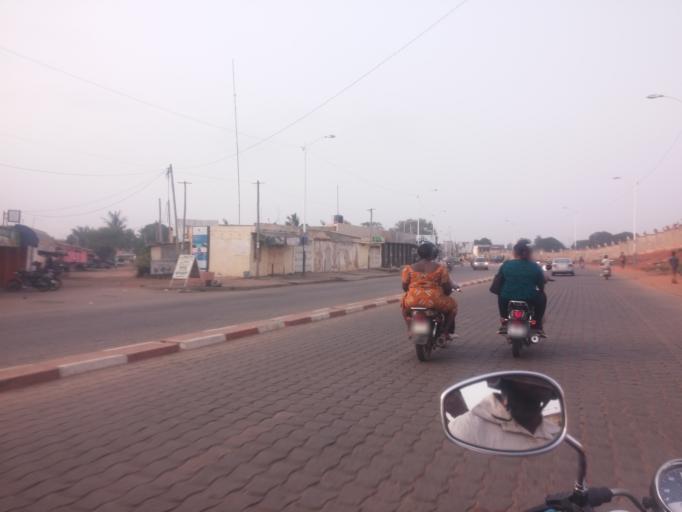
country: TG
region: Maritime
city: Lome
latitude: 6.1539
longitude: 1.2459
